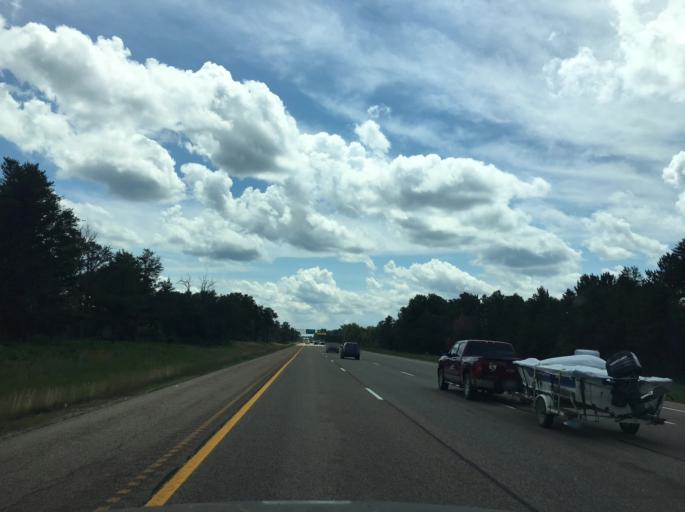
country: US
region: Michigan
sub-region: Crawford County
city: Grayling
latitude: 44.5948
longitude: -84.7095
